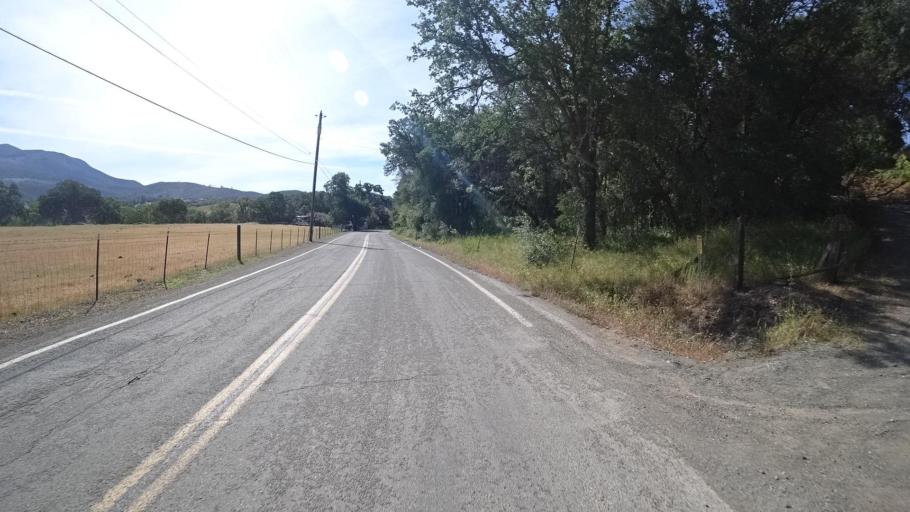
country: US
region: California
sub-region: Lake County
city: Kelseyville
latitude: 38.9638
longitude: -122.8384
